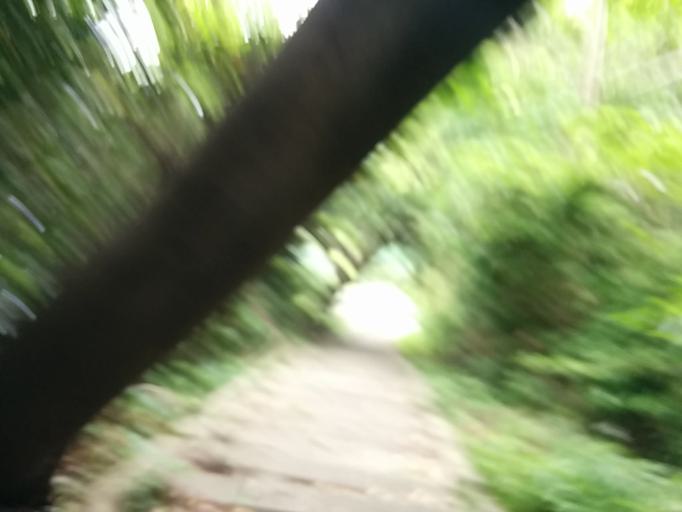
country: JP
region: Kyoto
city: Miyazu
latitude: 35.7752
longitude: 135.2238
